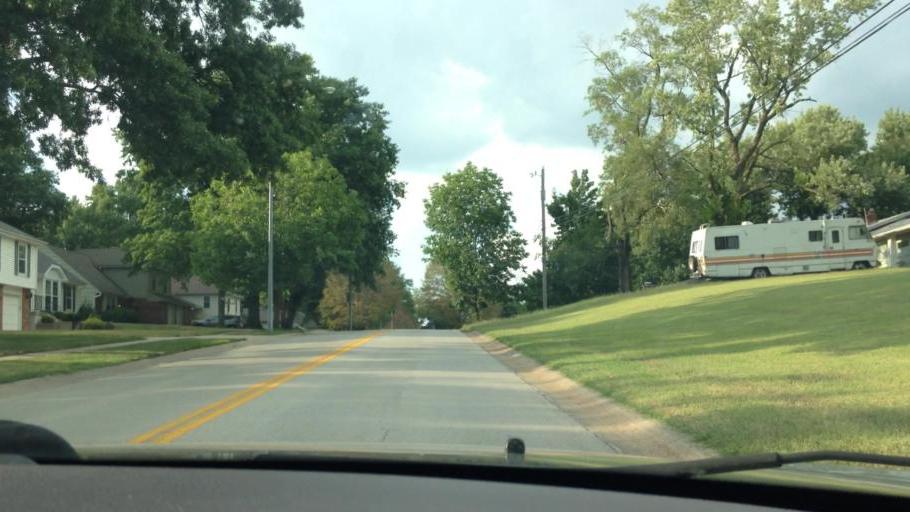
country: US
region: Missouri
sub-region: Platte County
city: Parkville
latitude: 39.2186
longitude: -94.6405
